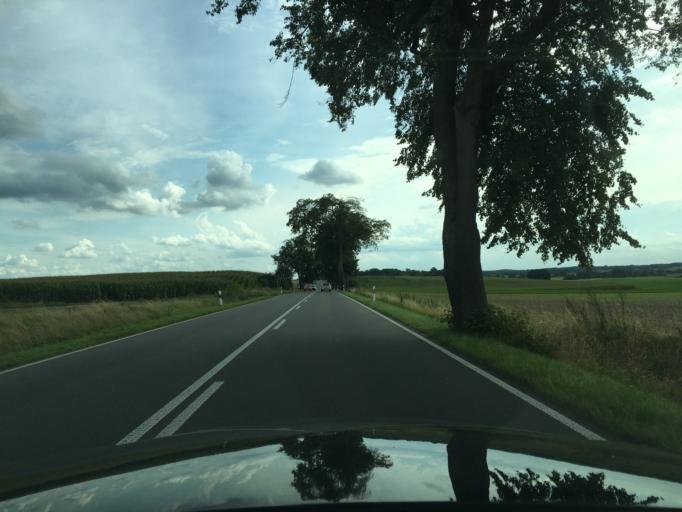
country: DE
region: Mecklenburg-Vorpommern
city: Penzlin
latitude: 53.4595
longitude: 13.0599
